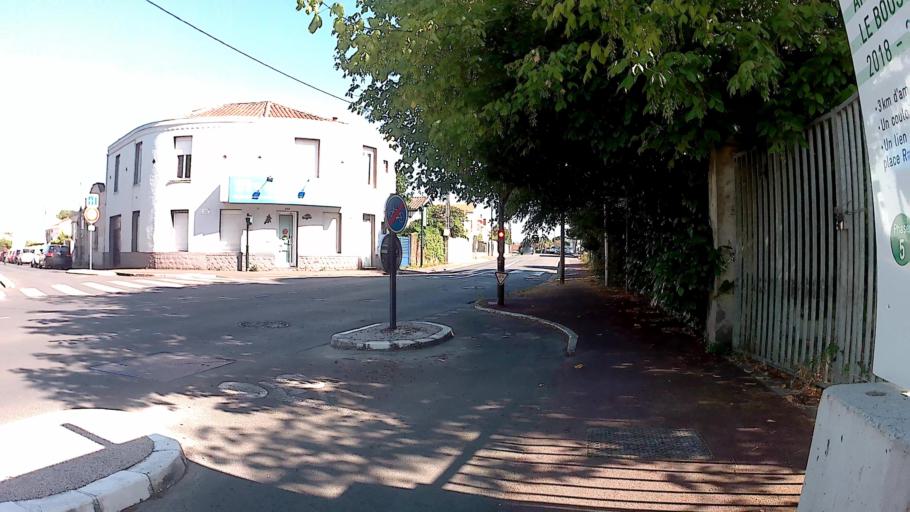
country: FR
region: Aquitaine
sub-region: Departement de la Gironde
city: Le Bouscat
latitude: 44.8730
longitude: -0.5999
